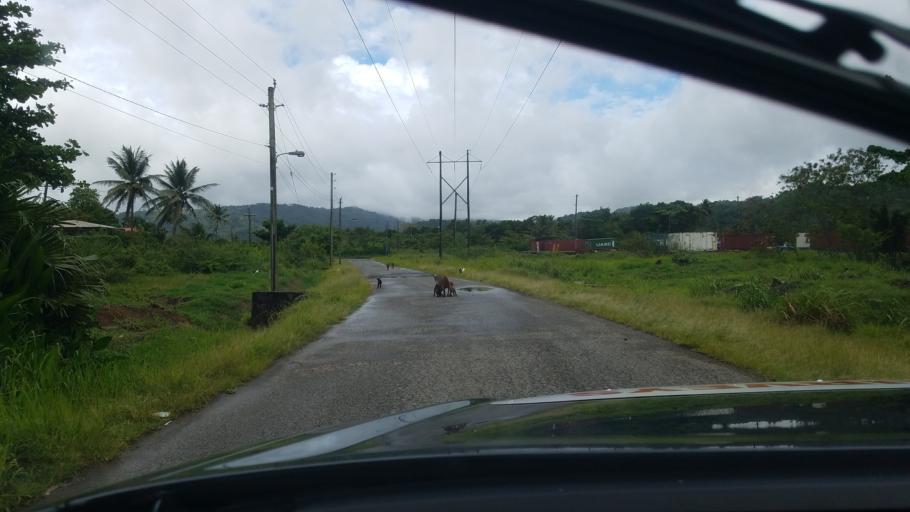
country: LC
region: Castries Quarter
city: Castries
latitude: 13.9863
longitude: -60.9990
